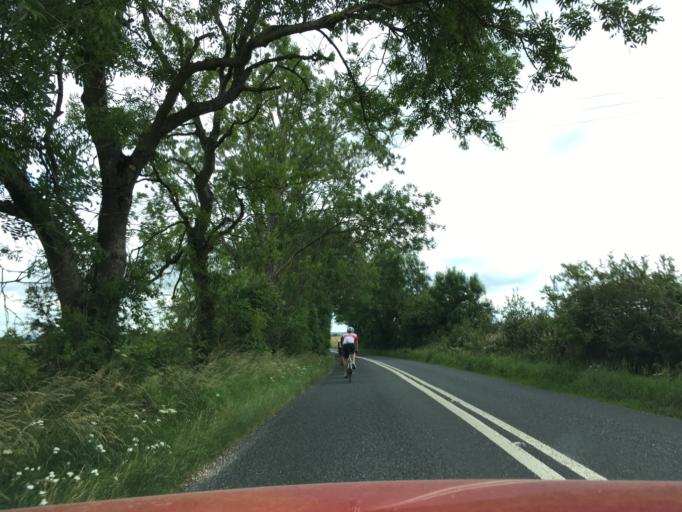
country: GB
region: England
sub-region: Gloucestershire
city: Westfield
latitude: 51.8875
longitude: -1.8437
